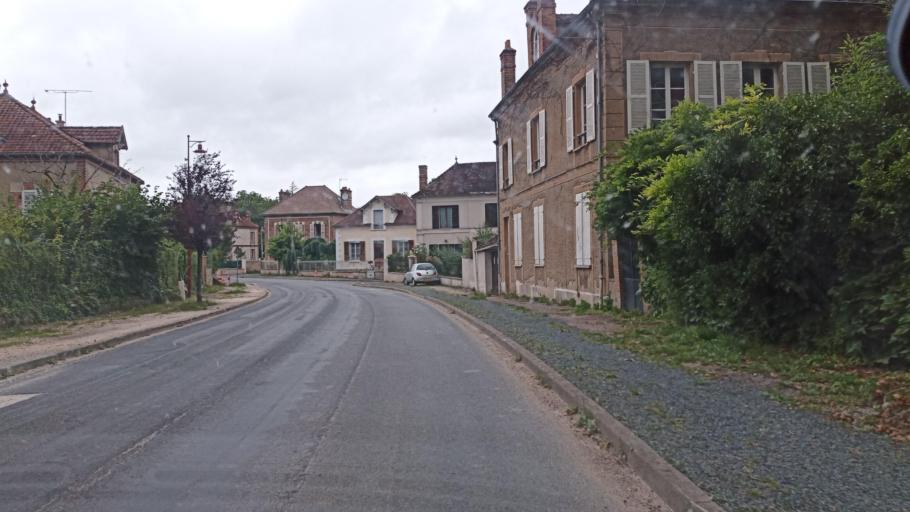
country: FR
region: Ile-de-France
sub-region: Departement de Seine-et-Marne
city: Voulx
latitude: 48.2831
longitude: 2.9692
